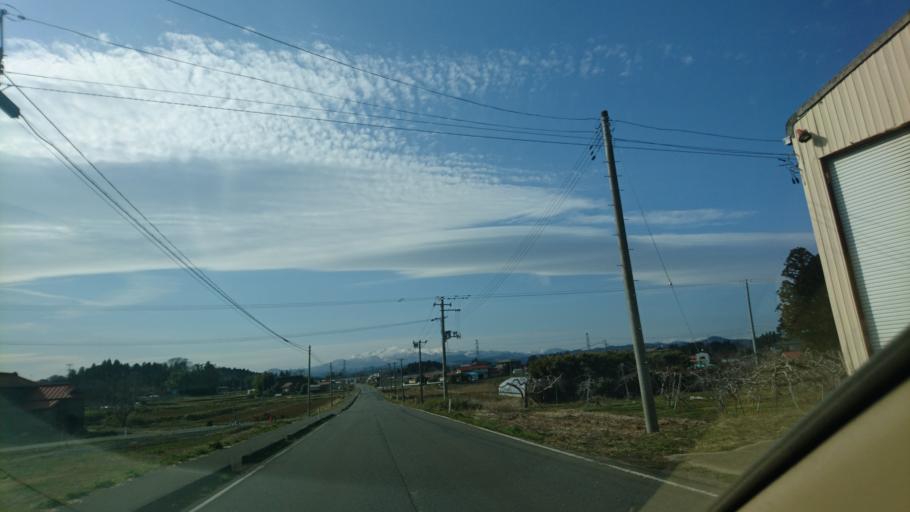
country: JP
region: Iwate
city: Ichinoseki
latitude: 38.8047
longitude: 141.0414
